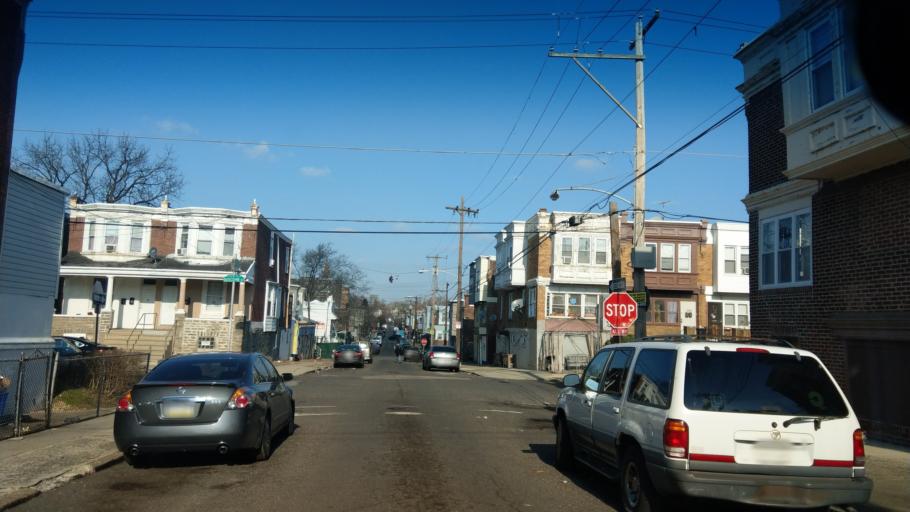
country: US
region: Pennsylvania
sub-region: Montgomery County
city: Rockledge
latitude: 40.0267
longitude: -75.1297
